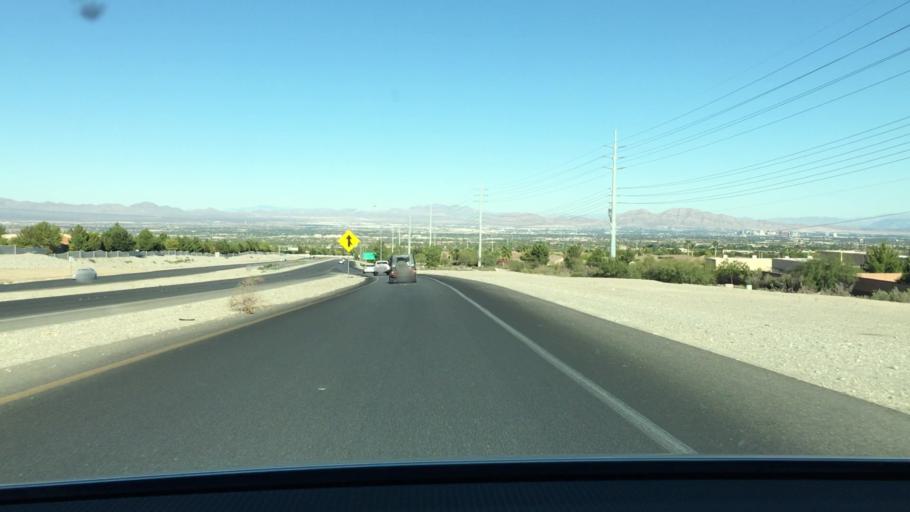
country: US
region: Nevada
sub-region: Clark County
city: Summerlin South
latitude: 36.1912
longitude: -115.3380
